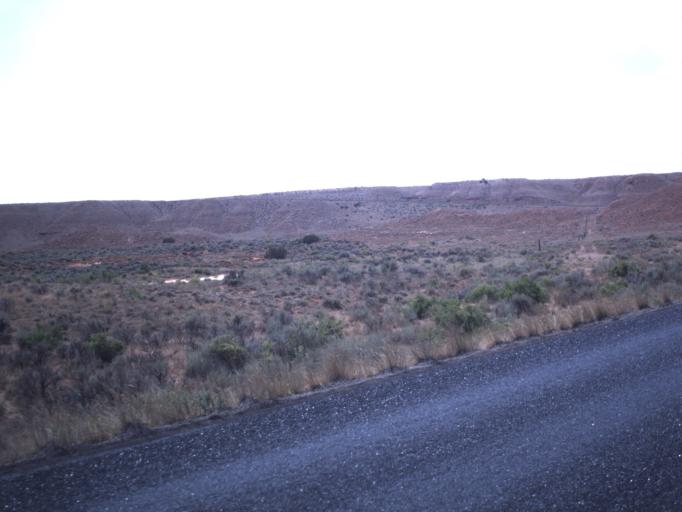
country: US
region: Utah
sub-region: Uintah County
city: Maeser
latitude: 40.4159
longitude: -109.7560
